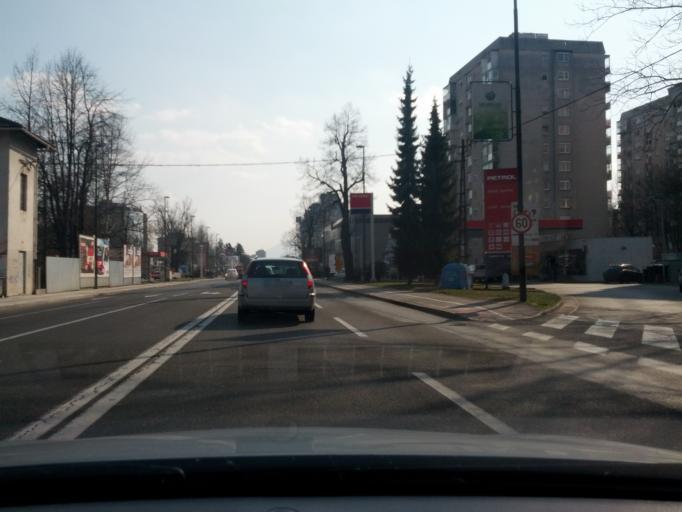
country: SI
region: Ljubljana
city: Ljubljana
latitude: 46.0795
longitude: 14.5126
